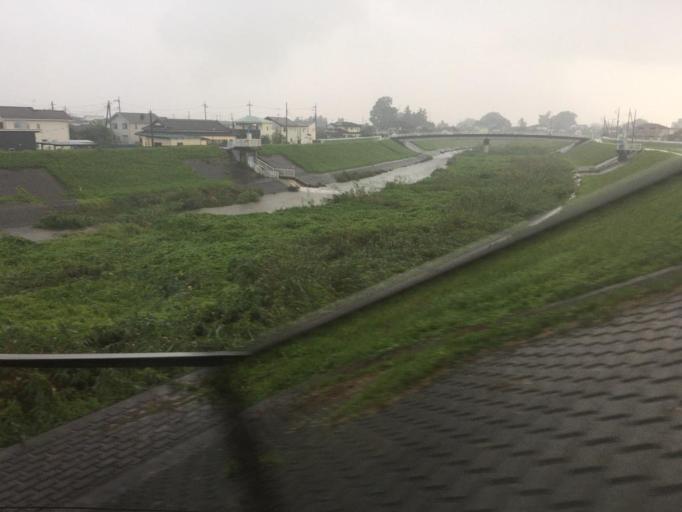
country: JP
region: Gunma
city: Tatebayashi
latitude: 36.2760
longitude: 139.4965
